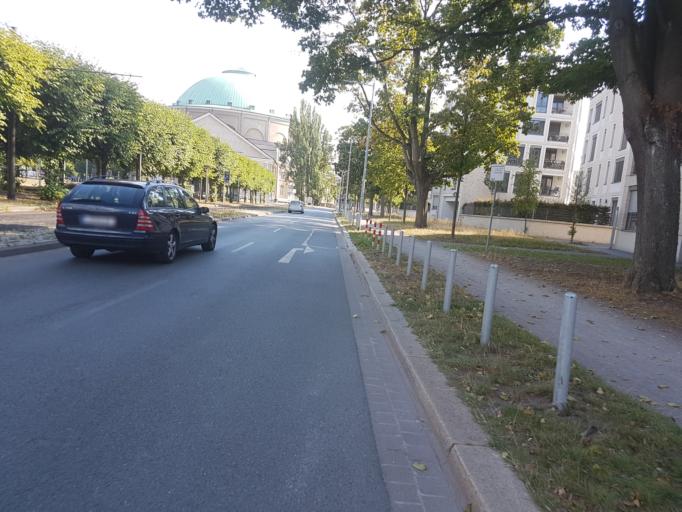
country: DE
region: Lower Saxony
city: Hannover
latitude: 52.3777
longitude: 9.7681
